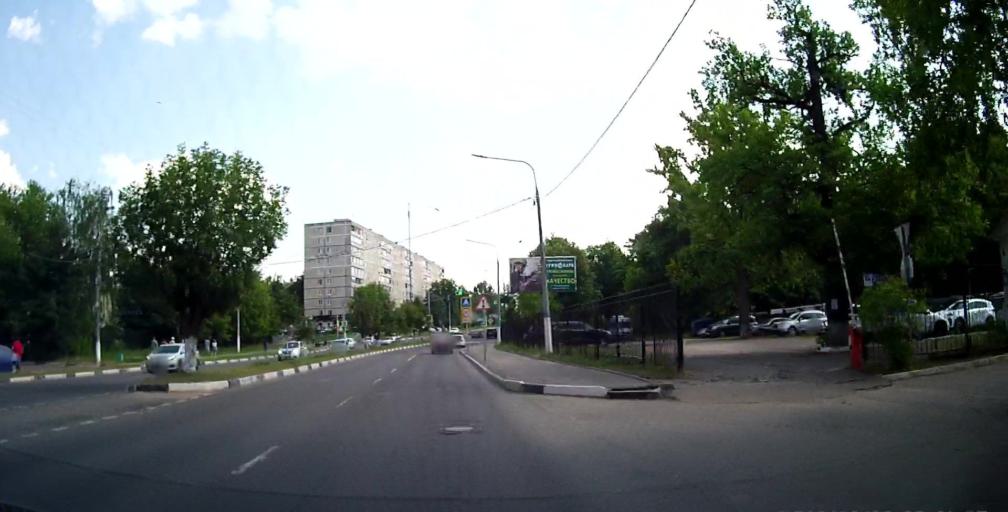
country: RU
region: Moskovskaya
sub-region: Podol'skiy Rayon
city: Podol'sk
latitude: 55.4197
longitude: 37.5185
